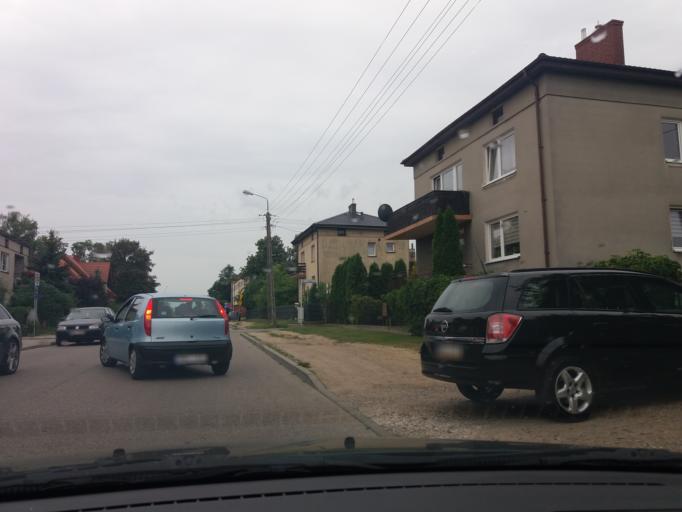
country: PL
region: Masovian Voivodeship
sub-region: Powiat mlawski
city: Mlawa
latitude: 53.1246
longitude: 20.3734
